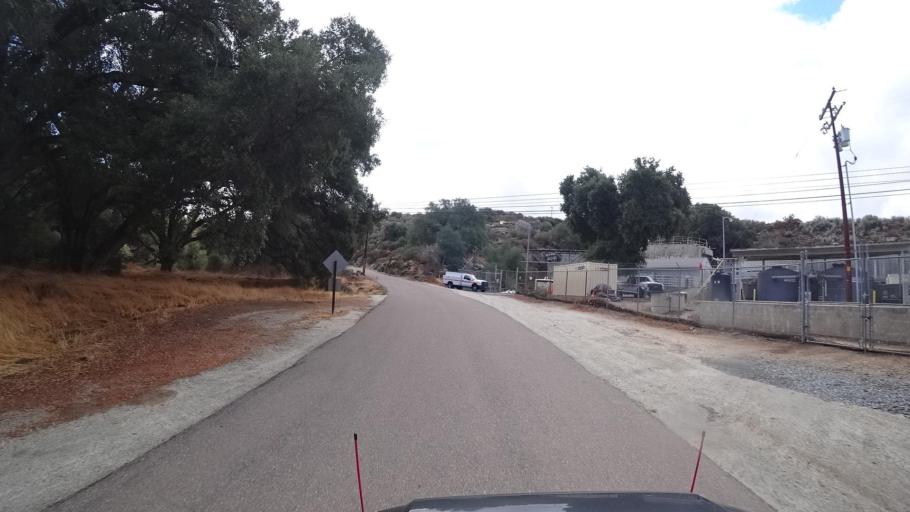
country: US
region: California
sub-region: San Diego County
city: Campo
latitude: 32.6077
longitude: -116.4792
